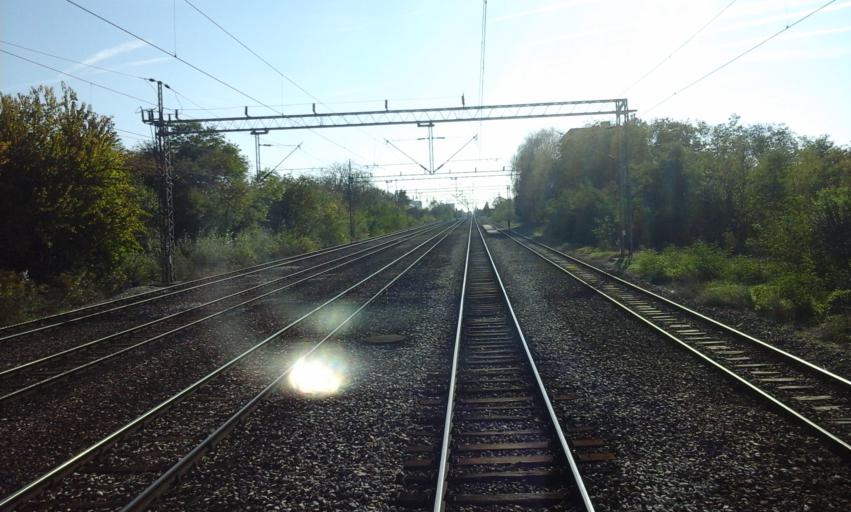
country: RS
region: Autonomna Pokrajina Vojvodina
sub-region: Severnobacki Okrug
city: Subotica
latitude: 46.0248
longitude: 19.6814
